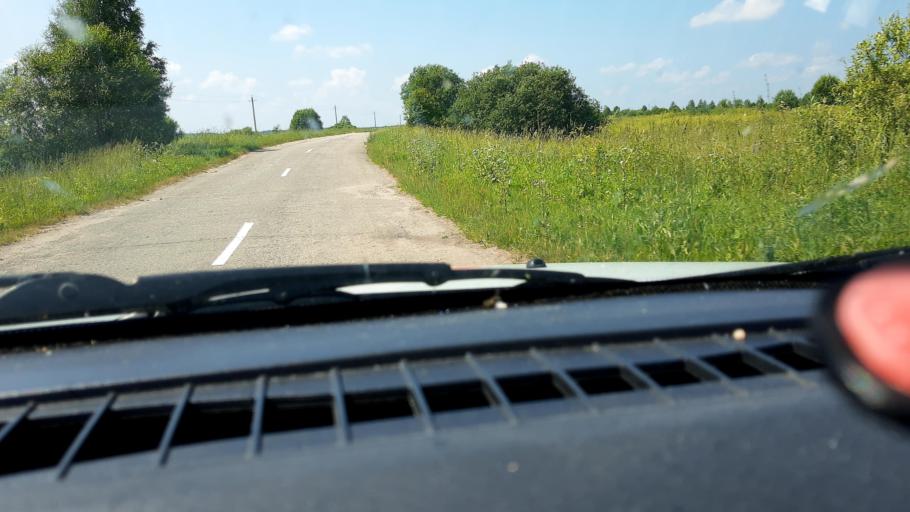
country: RU
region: Nizjnij Novgorod
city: Sharanga
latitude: 57.0677
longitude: 46.6821
